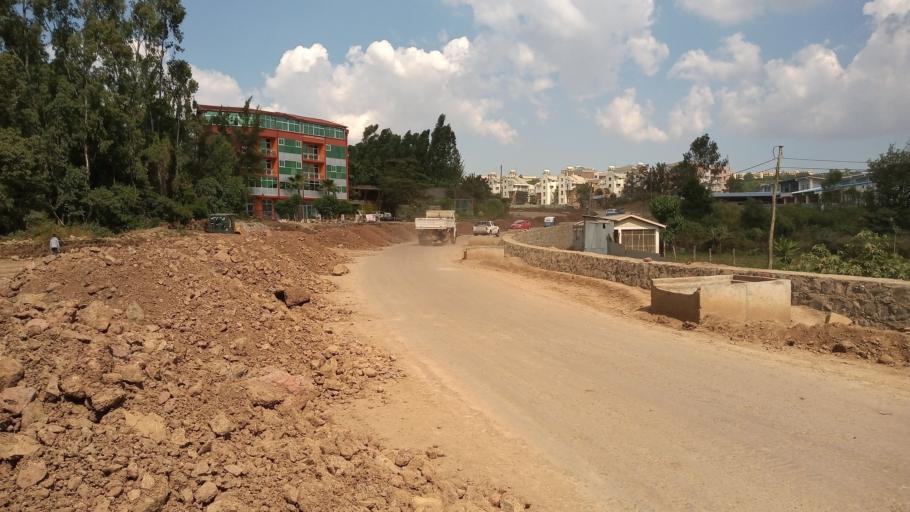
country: ET
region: Amhara
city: Gondar
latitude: 12.5855
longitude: 37.4347
